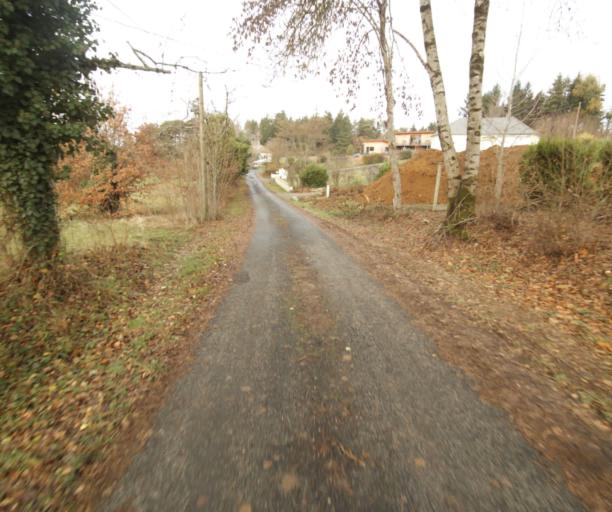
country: FR
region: Limousin
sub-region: Departement de la Correze
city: Saint-Mexant
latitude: 45.2656
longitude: 1.6239
